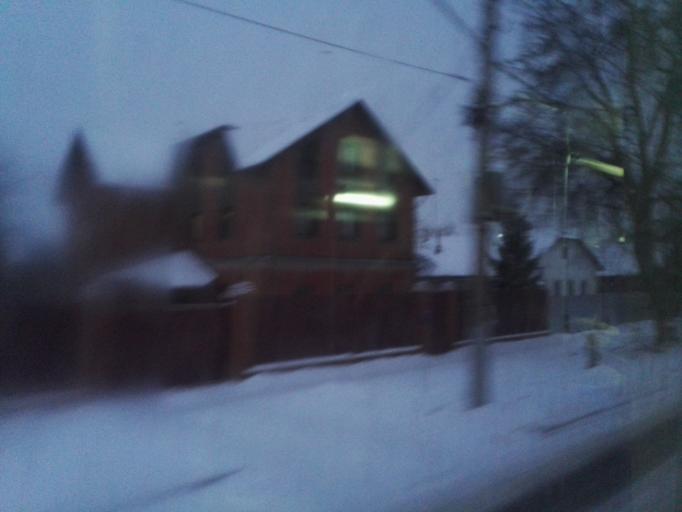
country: RU
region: Tula
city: Tula
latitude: 54.1692
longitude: 37.5998
